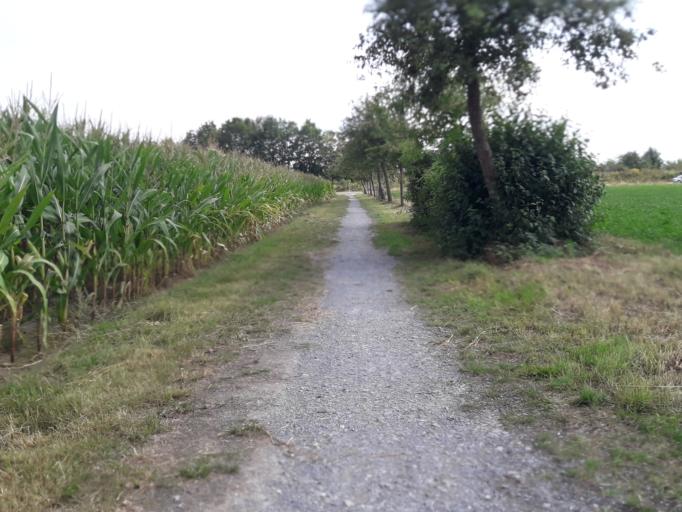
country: DE
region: North Rhine-Westphalia
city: Bad Lippspringe
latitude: 51.7720
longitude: 8.8121
